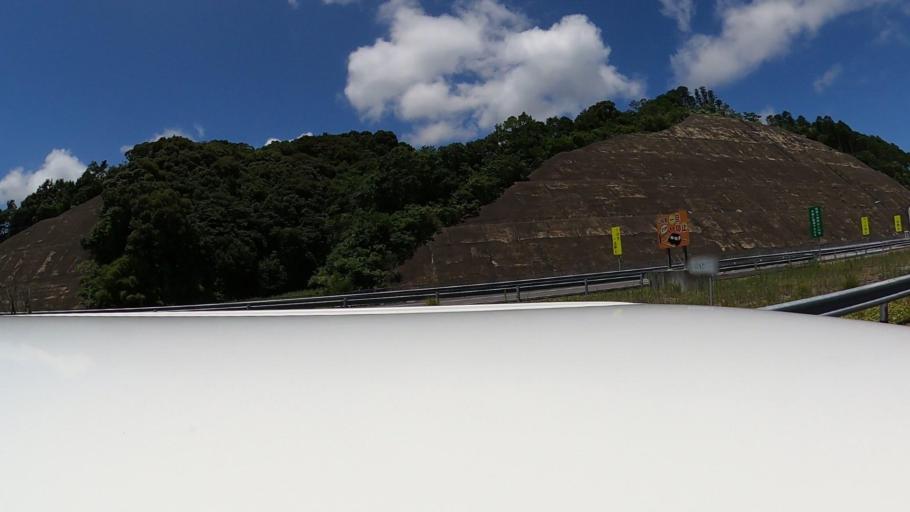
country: JP
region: Miyazaki
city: Nobeoka
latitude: 32.4916
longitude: 131.6520
